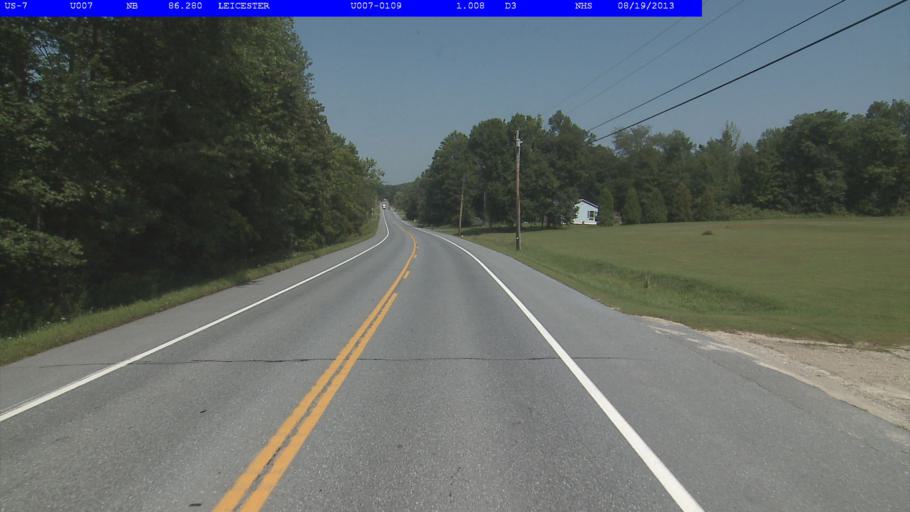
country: US
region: Vermont
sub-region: Rutland County
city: Brandon
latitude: 43.8579
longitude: -73.1062
